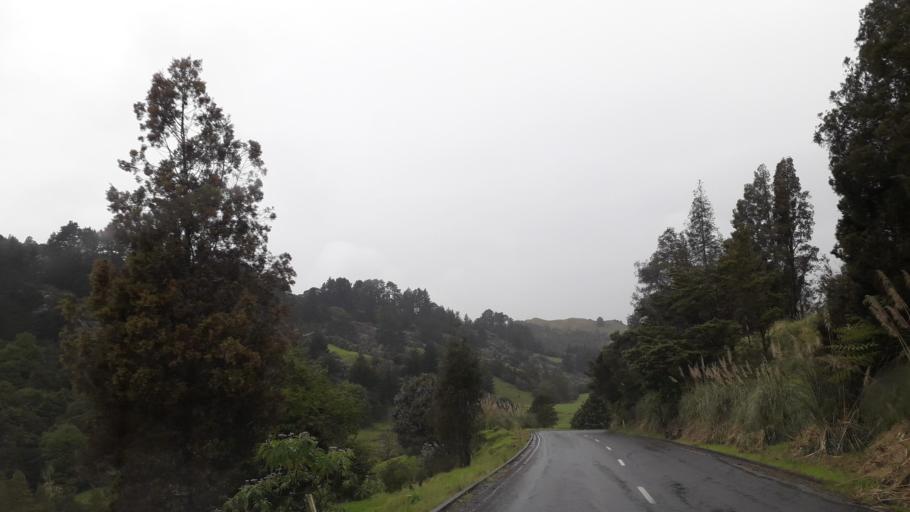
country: NZ
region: Northland
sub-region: Far North District
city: Kaitaia
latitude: -35.3575
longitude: 173.4669
